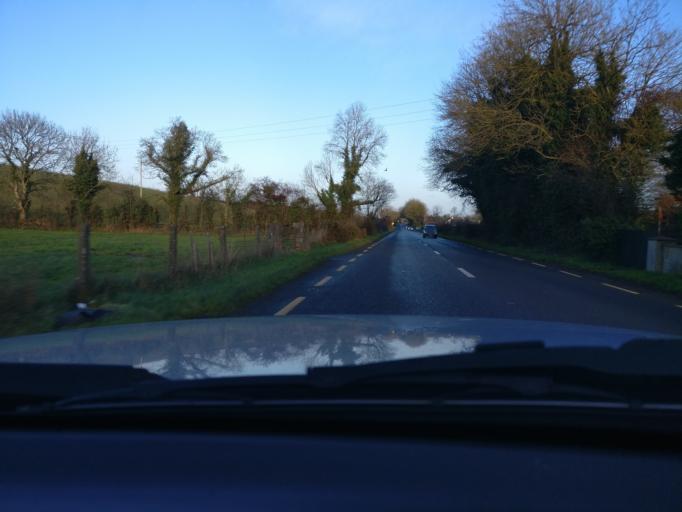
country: IE
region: Leinster
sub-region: Lu
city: Ardee
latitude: 53.8239
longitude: -6.6381
